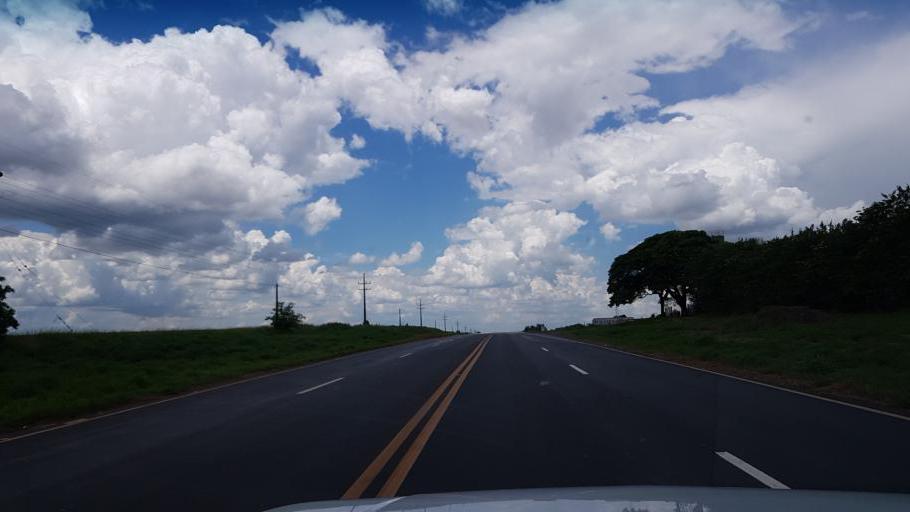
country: BR
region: Sao Paulo
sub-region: Paraguacu Paulista
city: Paraguacu Paulista
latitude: -22.3676
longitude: -50.6279
